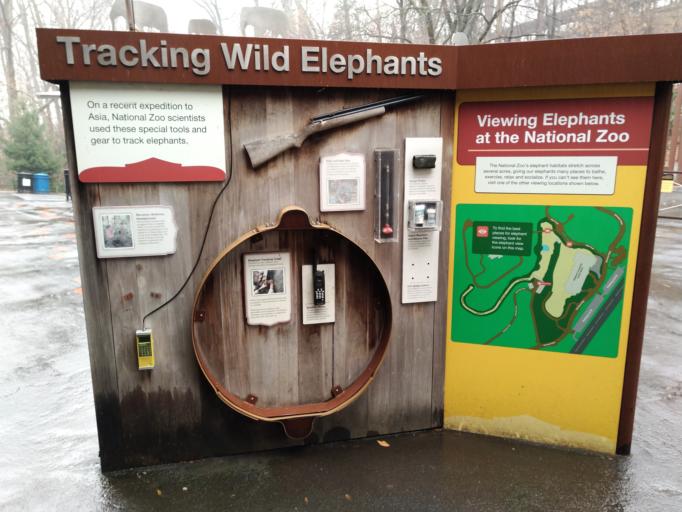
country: US
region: Washington, D.C.
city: Washington, D.C.
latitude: 38.9304
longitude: -77.0513
